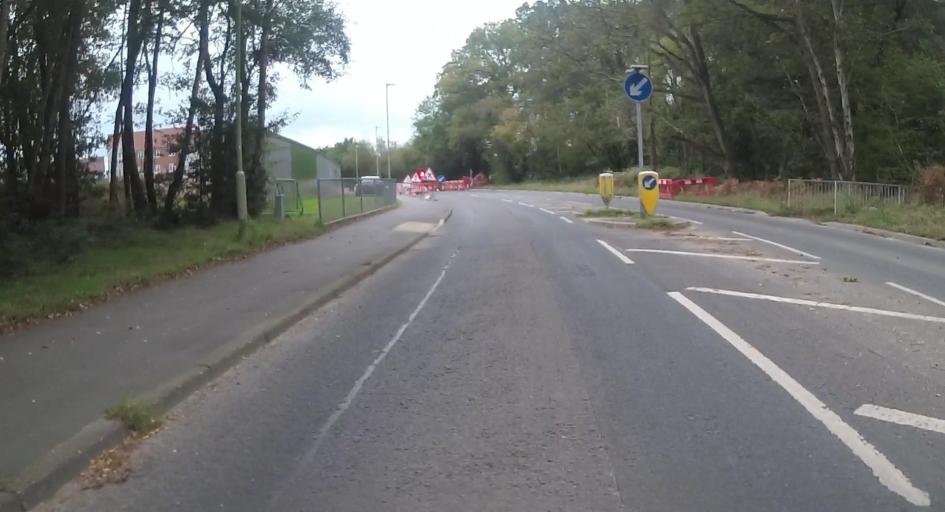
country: GB
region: England
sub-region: Hampshire
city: Fleet
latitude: 51.2750
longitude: -0.8638
